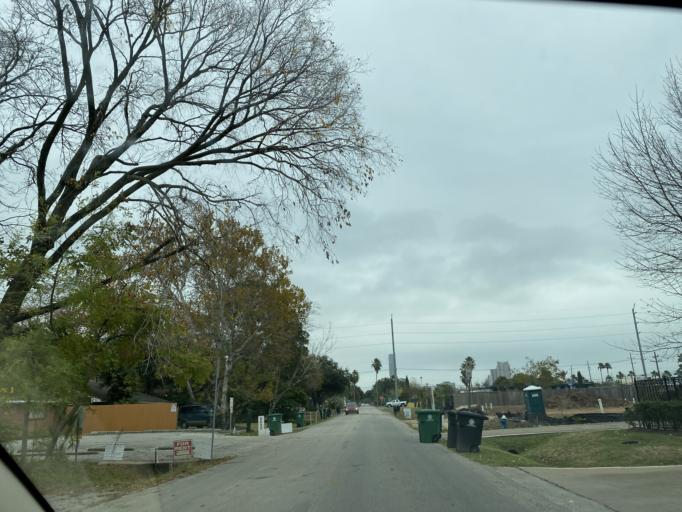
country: US
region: Texas
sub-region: Harris County
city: Bellaire
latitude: 29.7331
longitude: -95.4820
